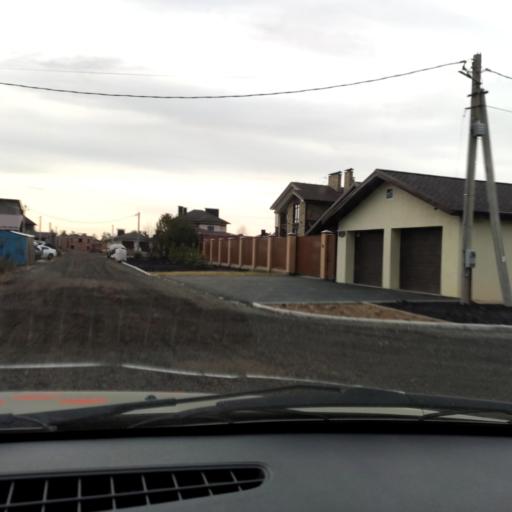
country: RU
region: Bashkortostan
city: Ufa
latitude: 54.6622
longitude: 55.9228
